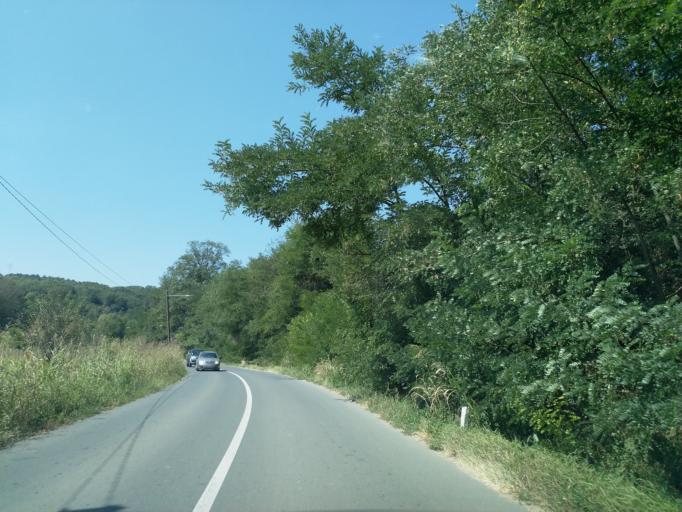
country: RS
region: Central Serbia
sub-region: Rasinski Okrug
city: Krusevac
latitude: 43.6269
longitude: 21.3364
